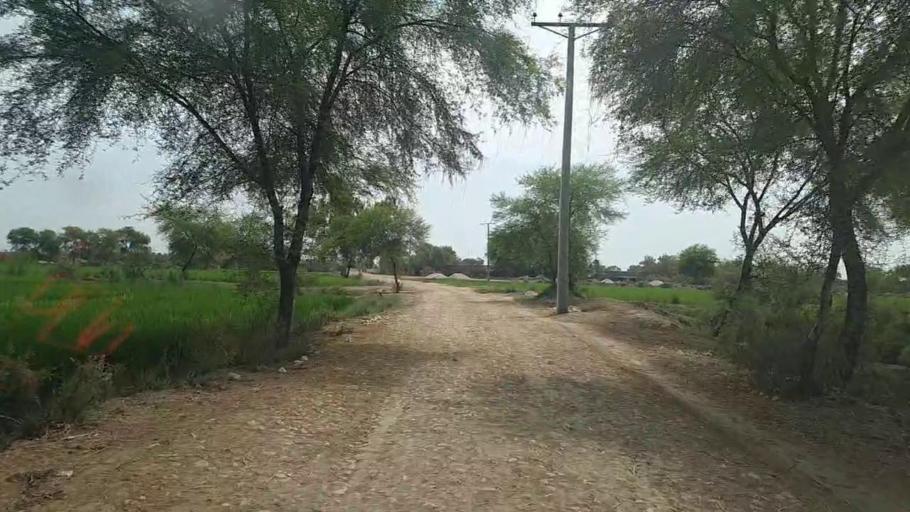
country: PK
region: Sindh
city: Thul
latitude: 28.2534
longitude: 68.6985
